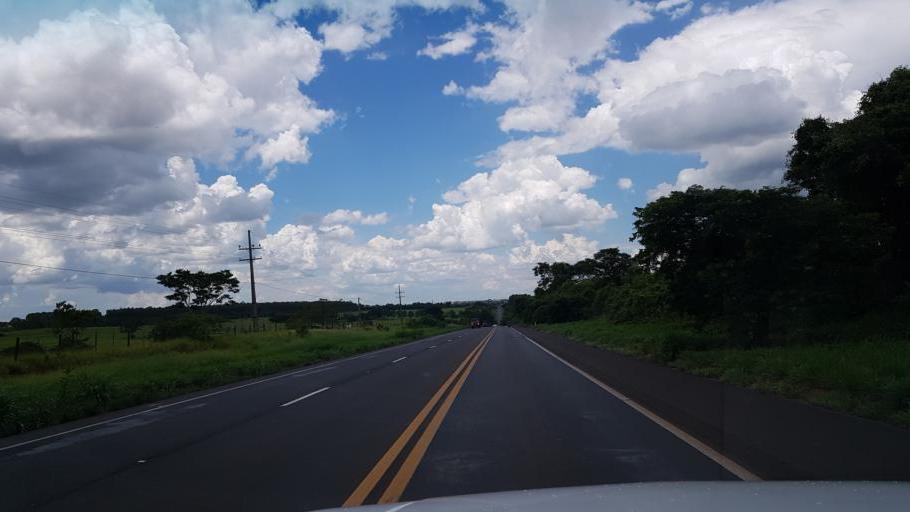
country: BR
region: Sao Paulo
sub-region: Paraguacu Paulista
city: Paraguacu Paulista
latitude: -22.3874
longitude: -50.6137
